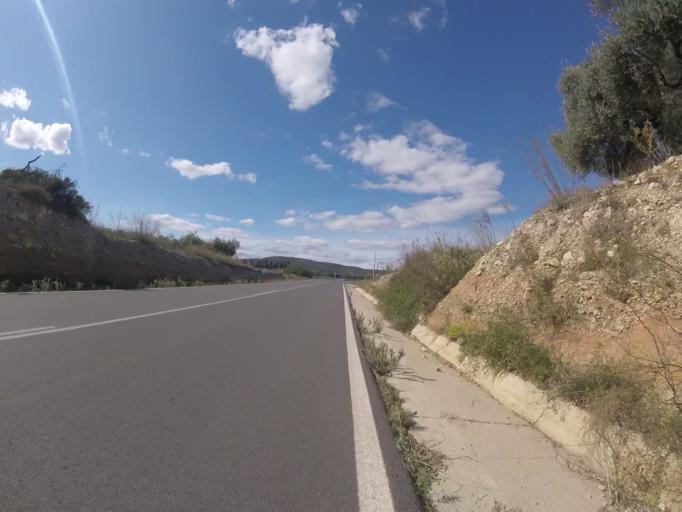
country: ES
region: Valencia
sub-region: Provincia de Castello
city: Chert/Xert
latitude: 40.4270
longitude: 0.1507
